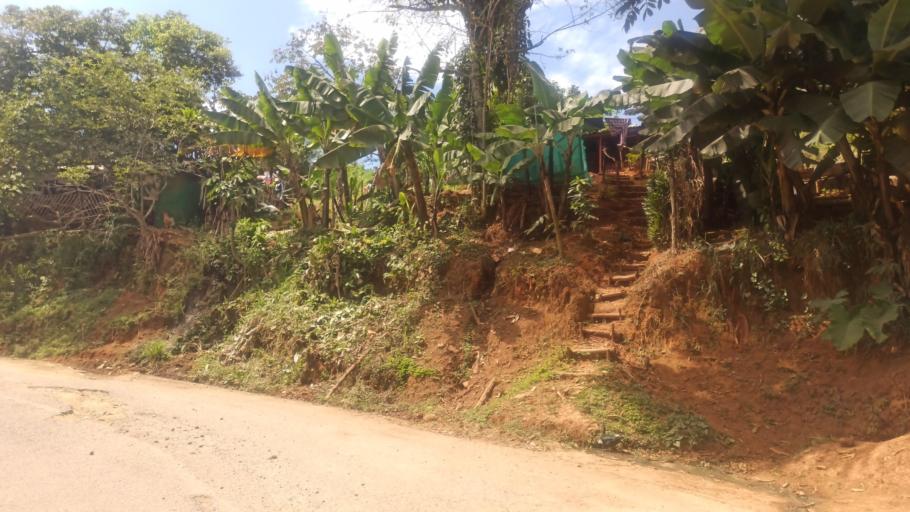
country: CO
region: Valle del Cauca
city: Jamundi
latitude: 3.1917
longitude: -76.6279
